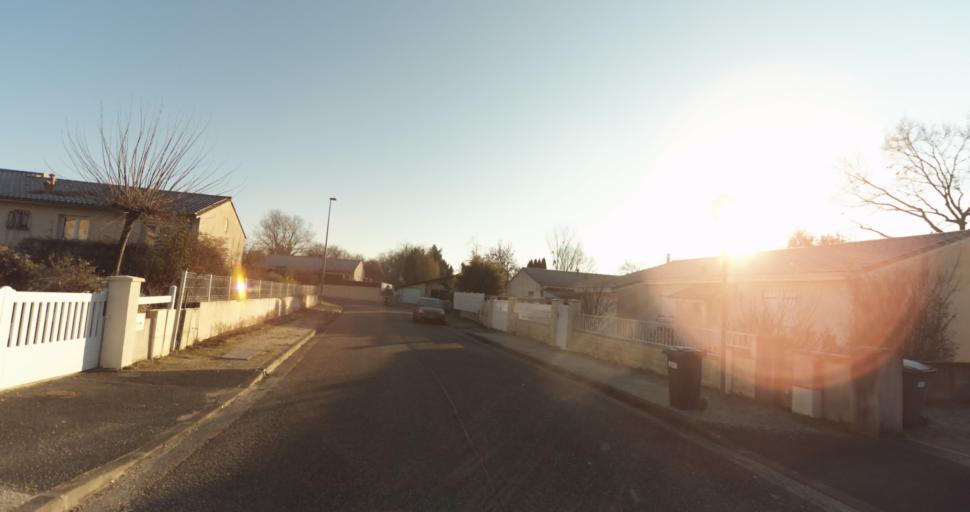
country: FR
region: Aquitaine
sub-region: Departement de la Gironde
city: Carbon-Blanc
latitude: 44.9017
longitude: -0.4998
